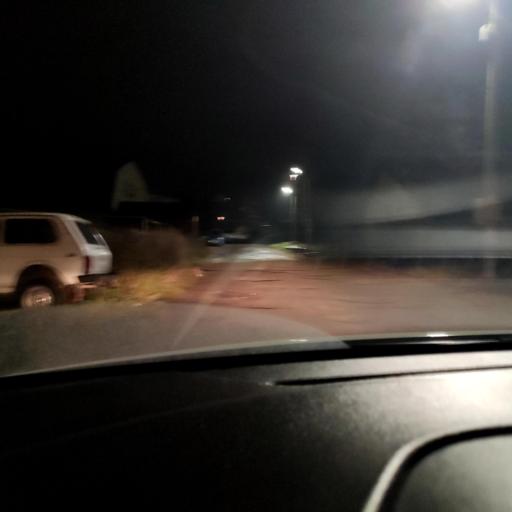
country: RU
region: Tatarstan
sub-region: Gorod Kazan'
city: Kazan
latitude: 55.8865
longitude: 49.0892
